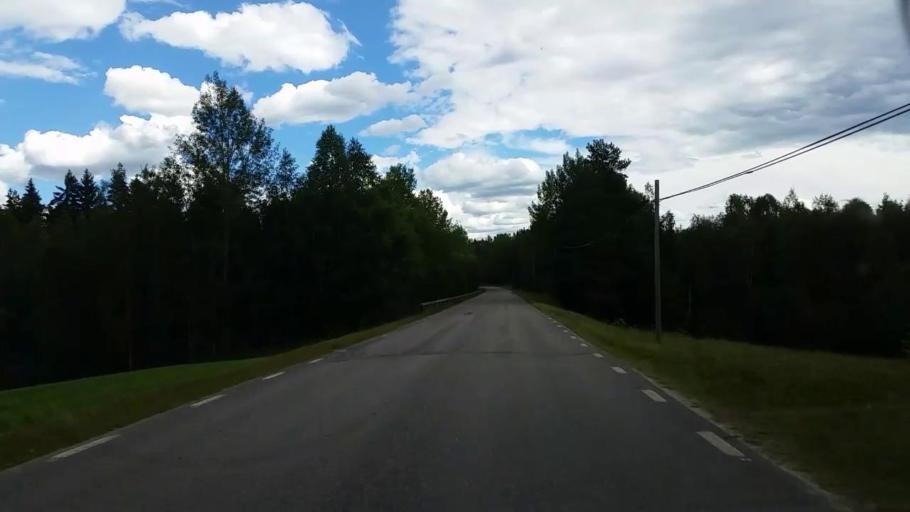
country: SE
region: Gaevleborg
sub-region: Ljusdals Kommun
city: Jaervsoe
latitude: 61.6710
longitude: 16.1287
